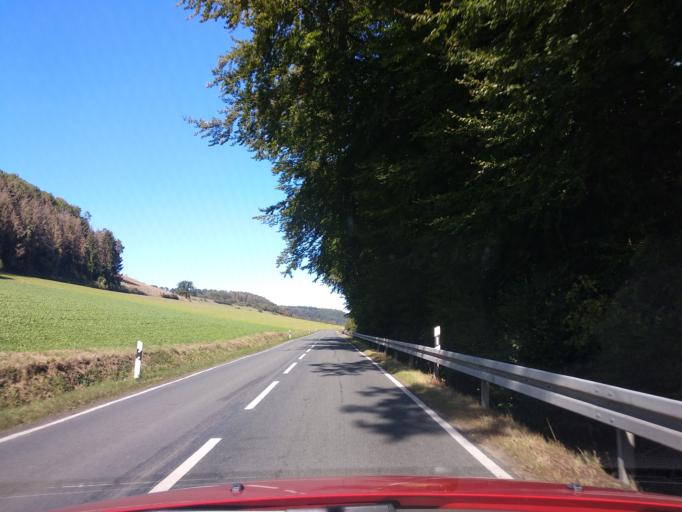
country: DE
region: North Rhine-Westphalia
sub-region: Regierungsbezirk Detmold
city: Hoexter
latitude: 51.7579
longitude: 9.2902
